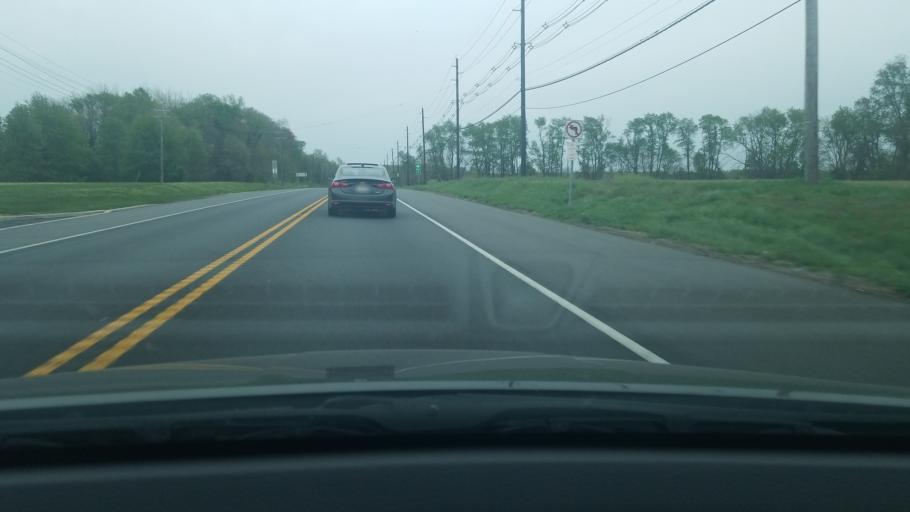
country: US
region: New Jersey
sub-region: Burlington County
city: Medford Lakes
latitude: 39.9030
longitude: -74.8055
